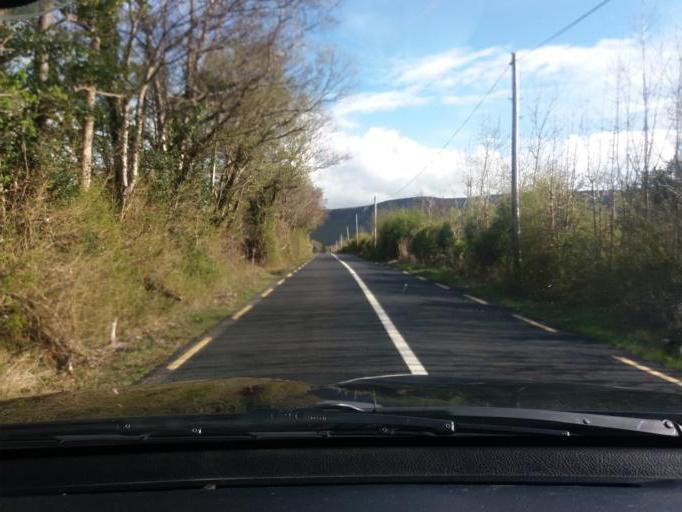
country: IE
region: Connaught
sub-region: County Leitrim
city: Kinlough
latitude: 54.3860
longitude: -8.2996
